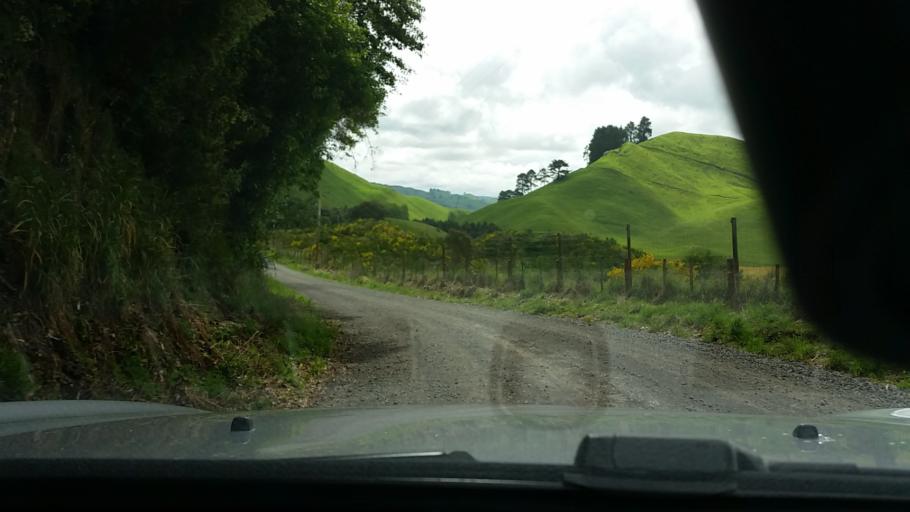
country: NZ
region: Bay of Plenty
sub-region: Rotorua District
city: Rotorua
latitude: -38.3986
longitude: 176.1785
